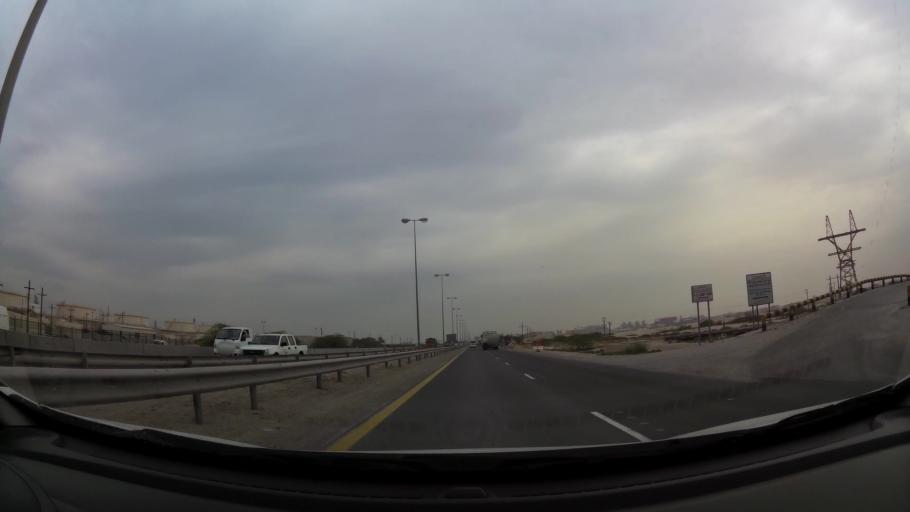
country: BH
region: Northern
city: Ar Rifa'
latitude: 26.1131
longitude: 50.5965
